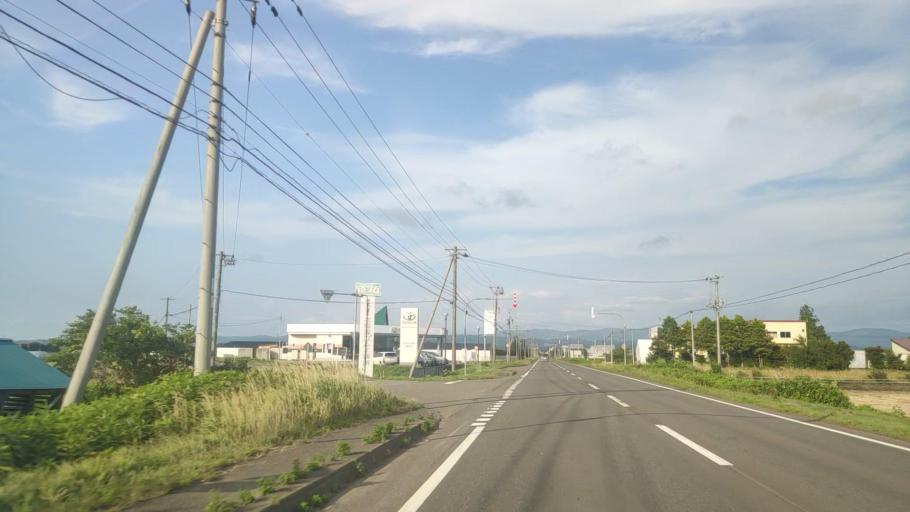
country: JP
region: Hokkaido
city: Iwamizawa
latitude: 43.0172
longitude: 141.7951
